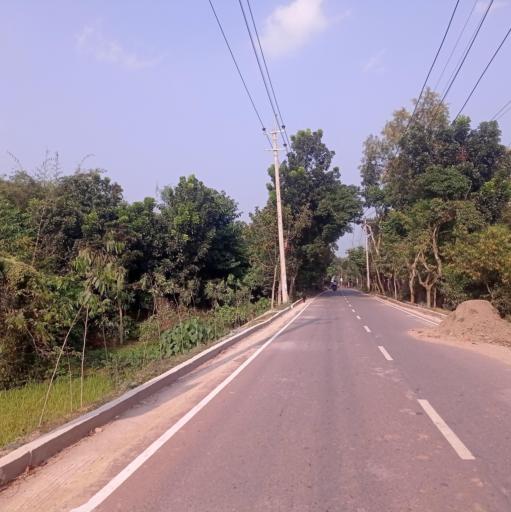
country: BD
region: Dhaka
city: Bhairab Bazar
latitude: 24.0601
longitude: 90.8395
